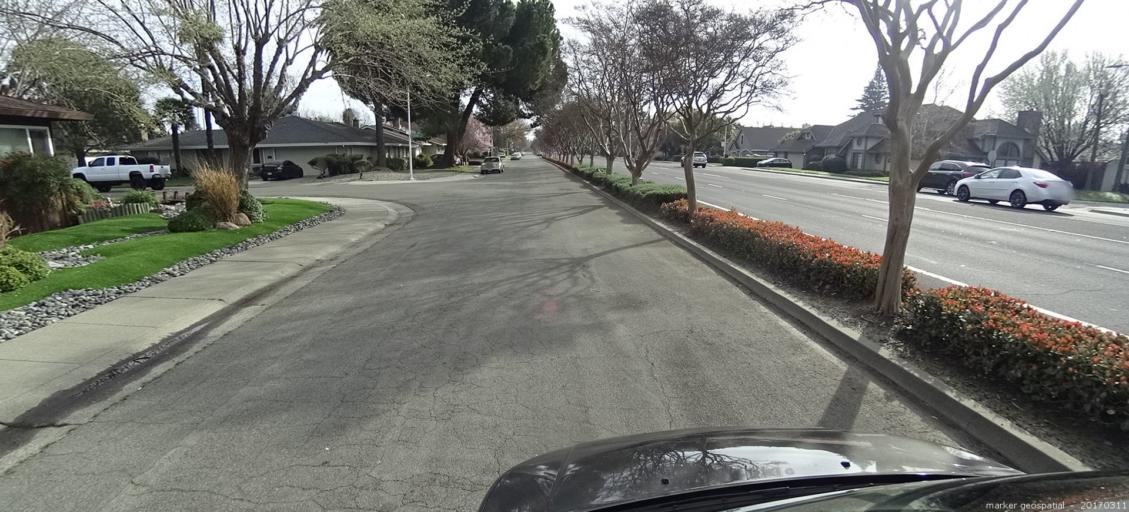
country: US
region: California
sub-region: Yolo County
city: West Sacramento
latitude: 38.5126
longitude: -121.5378
